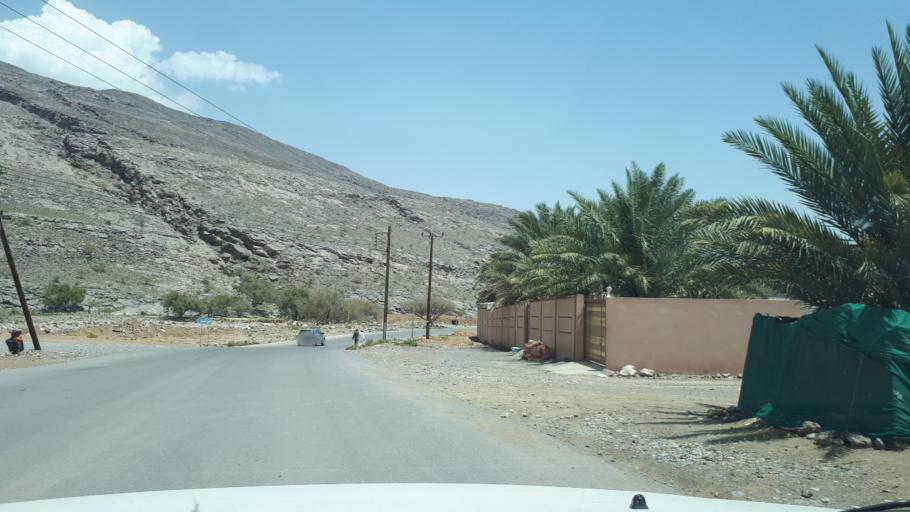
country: OM
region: Muhafazat ad Dakhiliyah
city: Bahla'
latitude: 23.1712
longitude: 57.1526
